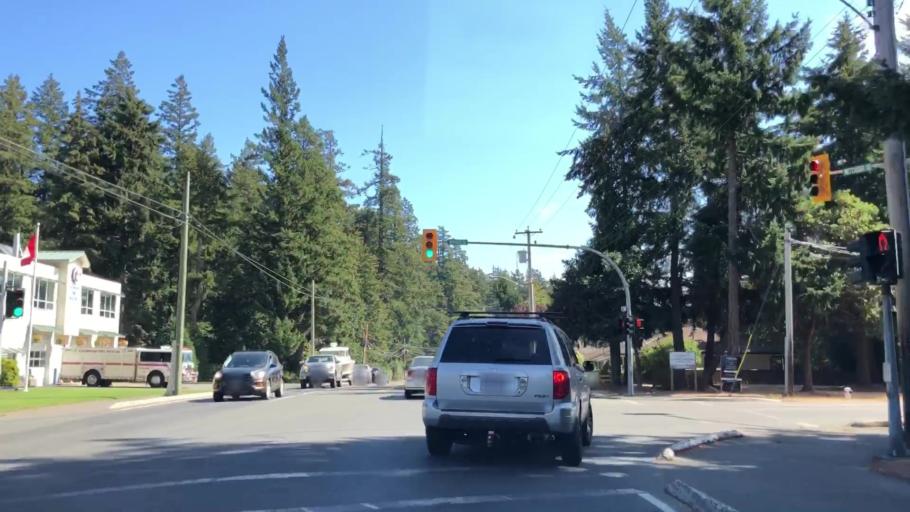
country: CA
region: British Columbia
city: Colwood
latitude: 48.4264
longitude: -123.4907
